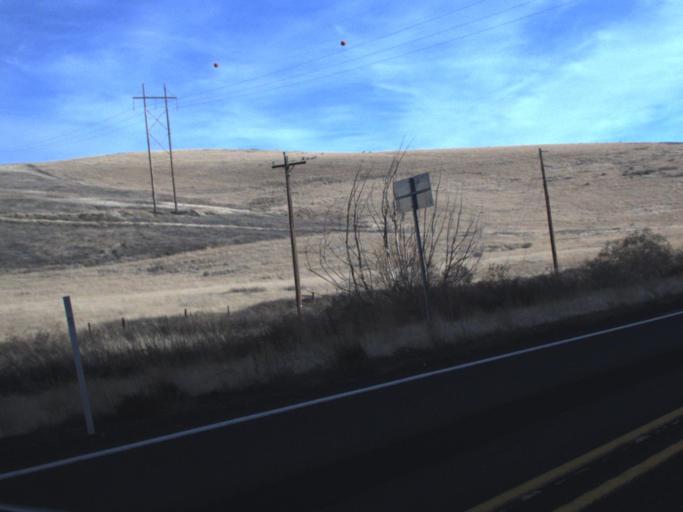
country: US
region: Washington
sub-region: Columbia County
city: Dayton
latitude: 46.4459
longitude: -117.9549
